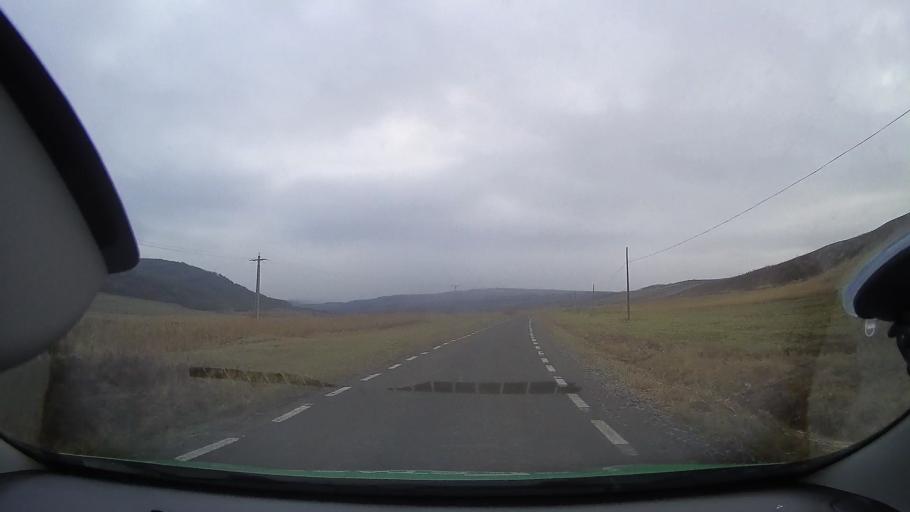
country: RO
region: Mures
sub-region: Comuna Bichis
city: Bichis
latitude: 46.3922
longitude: 24.0899
